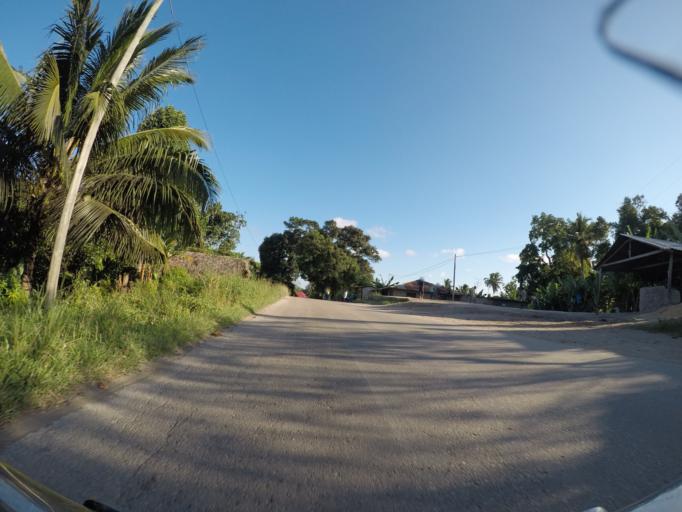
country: TZ
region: Pemba South
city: Mtambile
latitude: -5.3351
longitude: 39.7298
